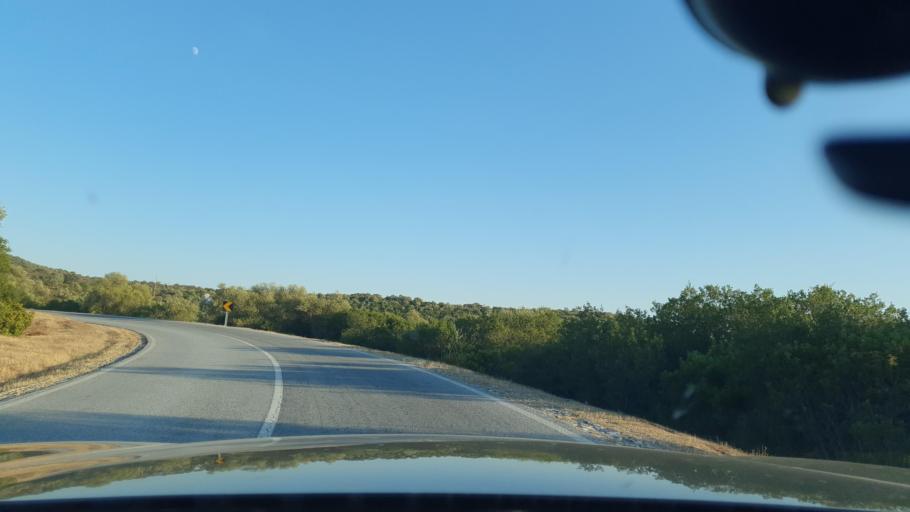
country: PT
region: Evora
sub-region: Estremoz
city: Estremoz
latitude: 38.9156
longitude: -7.6674
